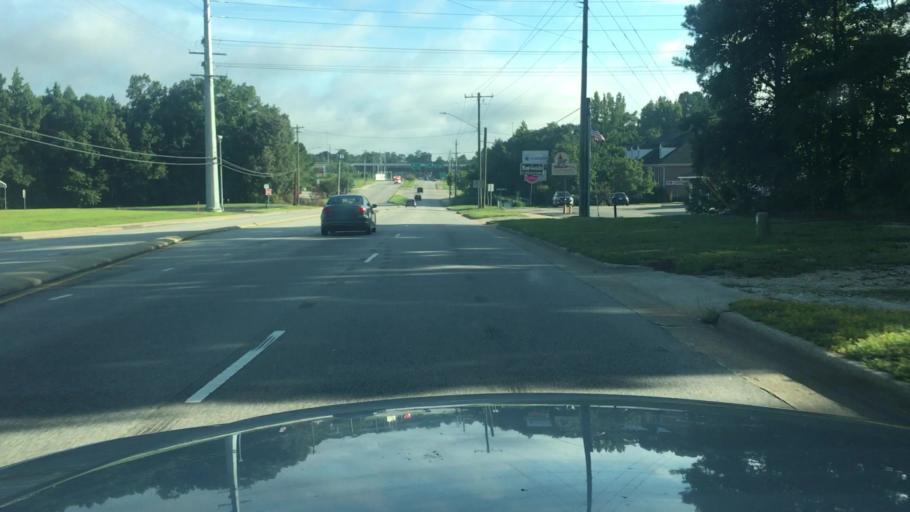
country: US
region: North Carolina
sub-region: Cumberland County
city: Eastover
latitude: 35.1494
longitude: -78.8709
